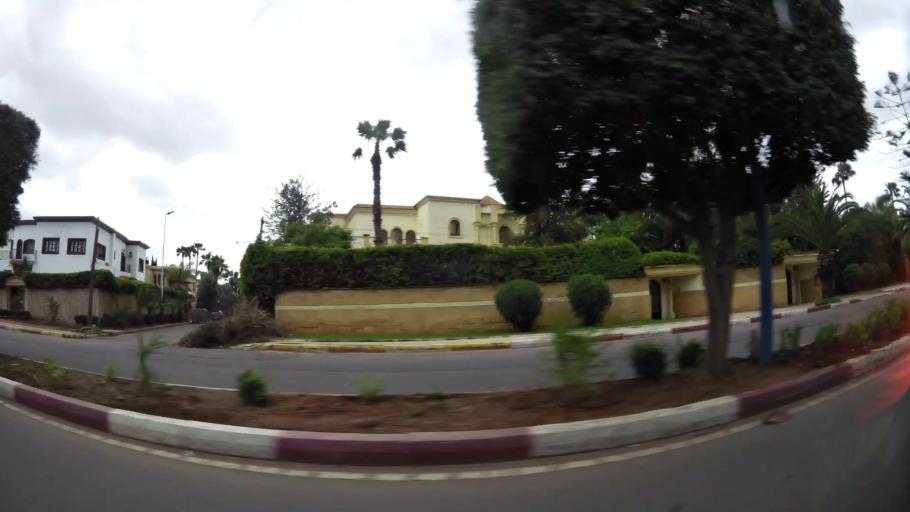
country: MA
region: Grand Casablanca
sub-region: Casablanca
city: Casablanca
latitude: 33.5335
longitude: -7.6296
